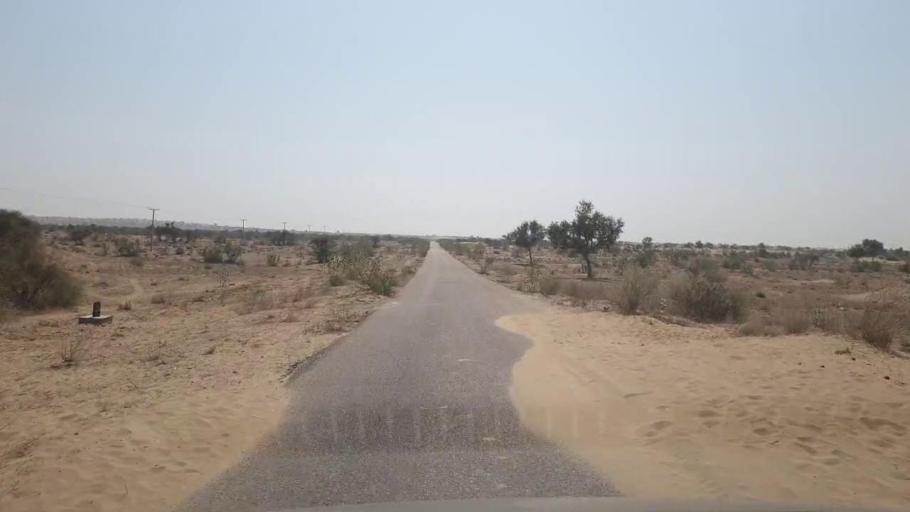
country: PK
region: Sindh
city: Chor
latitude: 25.6000
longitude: 70.1810
